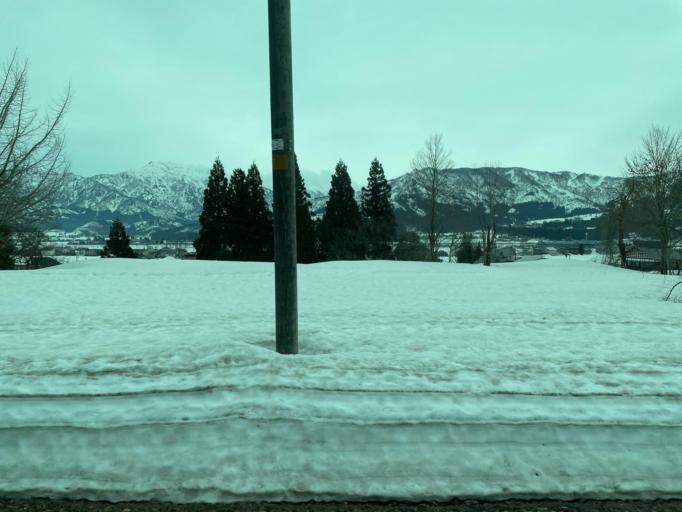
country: JP
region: Niigata
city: Shiozawa
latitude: 37.0106
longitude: 138.8127
